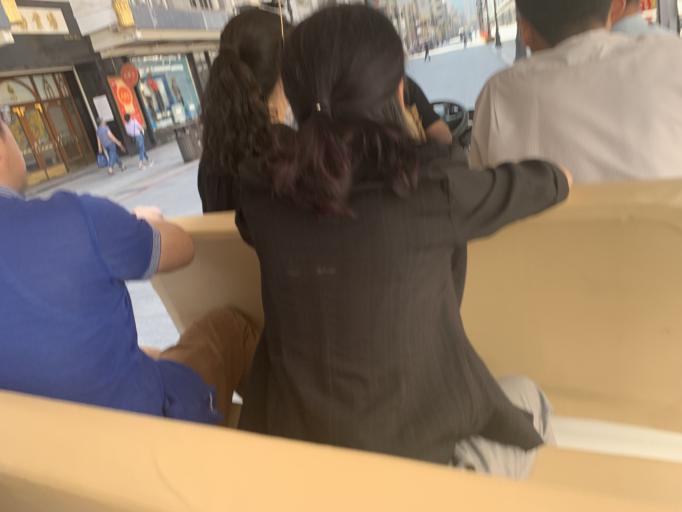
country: CN
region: Tianjin Shi
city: Quanyechang
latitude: 39.1260
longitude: 117.1951
